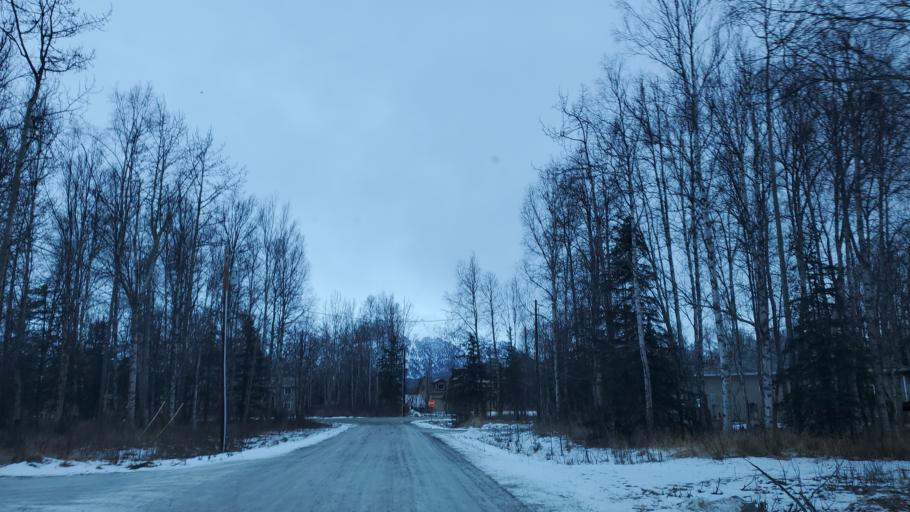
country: US
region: Alaska
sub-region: Matanuska-Susitna Borough
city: Lakes
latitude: 61.6665
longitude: -149.3018
